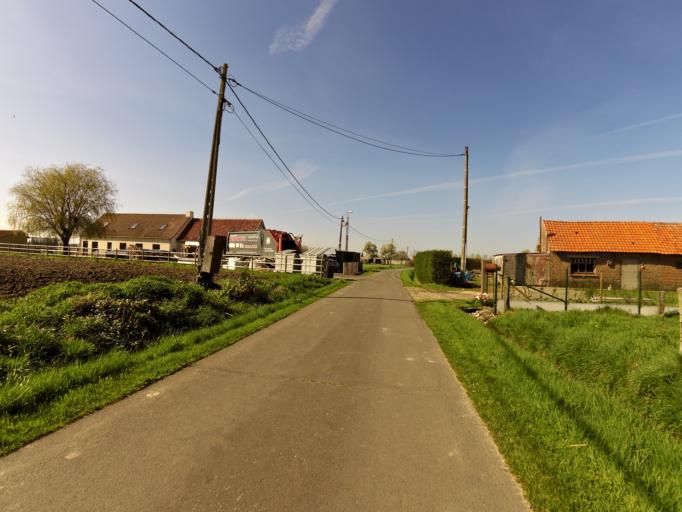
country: BE
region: Flanders
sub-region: Provincie West-Vlaanderen
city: Jabbeke
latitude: 51.1797
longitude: 3.0663
